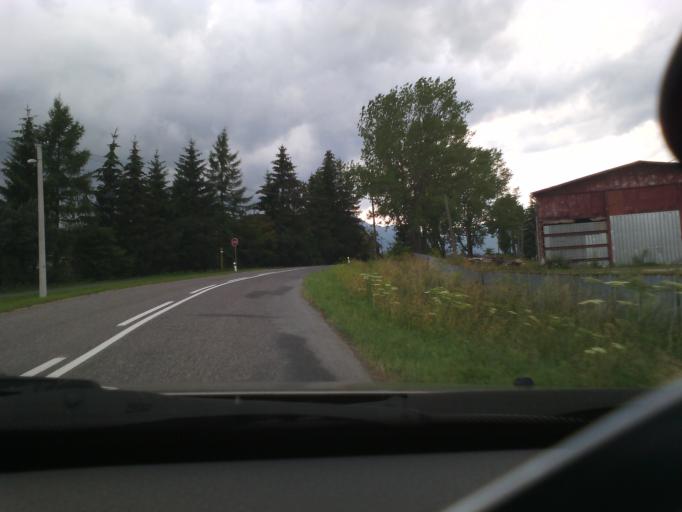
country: SK
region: Presovsky
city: Lubica
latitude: 49.0862
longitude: 20.4027
